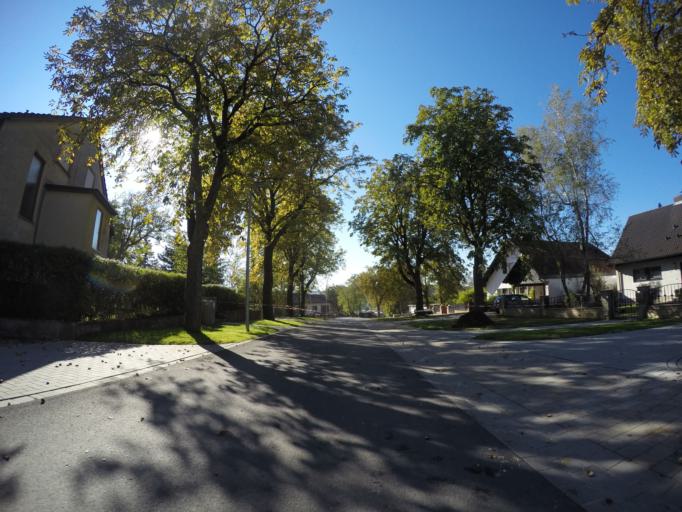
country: DE
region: Bavaria
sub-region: Regierungsbezirk Unterfranken
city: Remlingen
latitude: 49.8073
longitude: 9.6942
